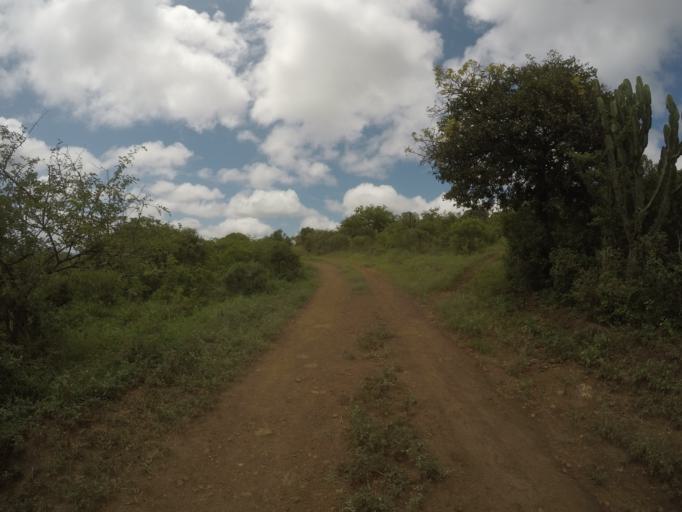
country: ZA
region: KwaZulu-Natal
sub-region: uThungulu District Municipality
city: Empangeni
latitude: -28.5780
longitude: 31.8250
